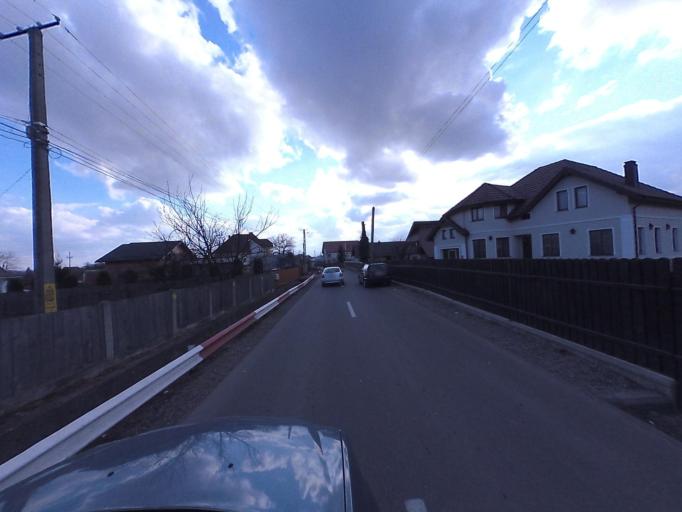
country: RO
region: Neamt
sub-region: Oras Targu Neamt
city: Targu Neamt
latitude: 47.2090
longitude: 26.3741
